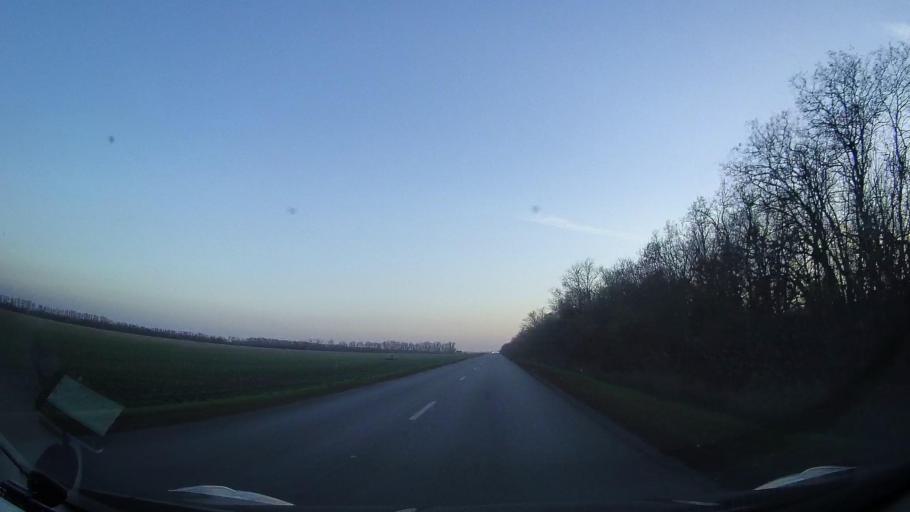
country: RU
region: Rostov
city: Zernograd
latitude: 47.0347
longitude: 40.3917
